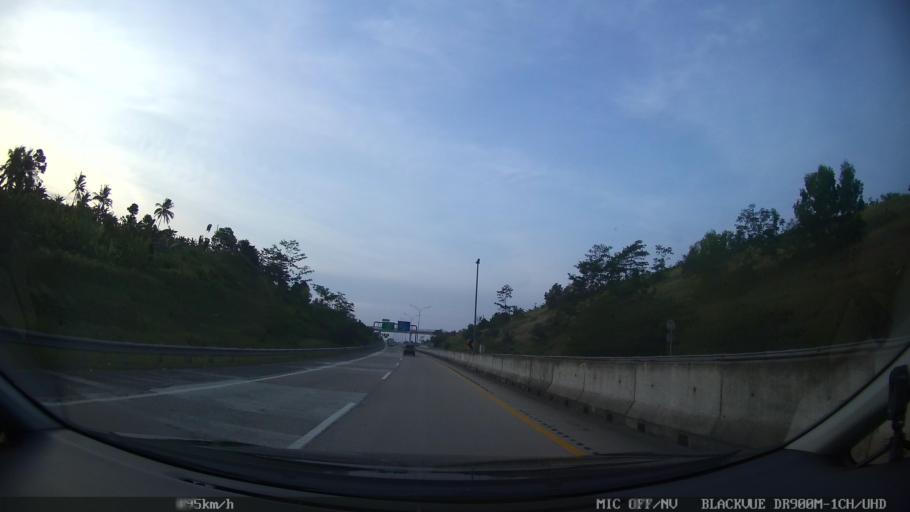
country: ID
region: Lampung
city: Penengahan
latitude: -5.8152
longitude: 105.7366
